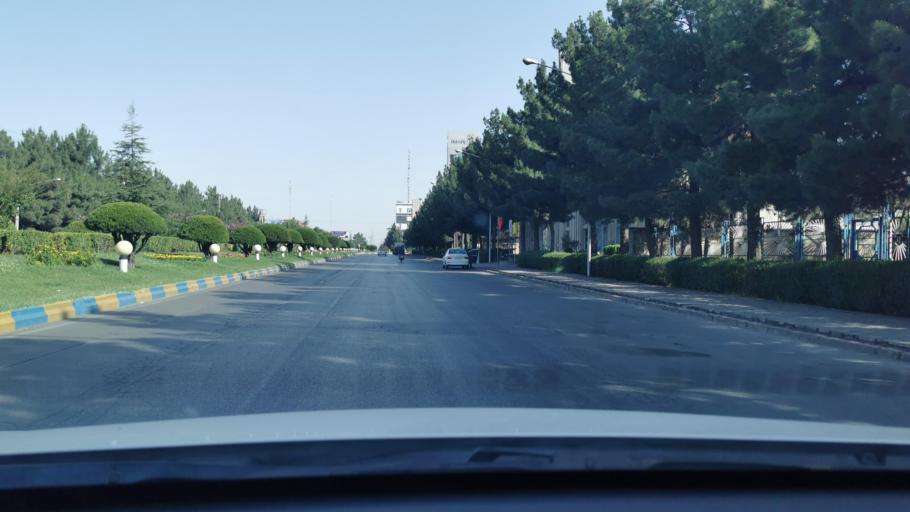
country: IR
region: Razavi Khorasan
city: Torqabeh
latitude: 36.4293
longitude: 59.4144
